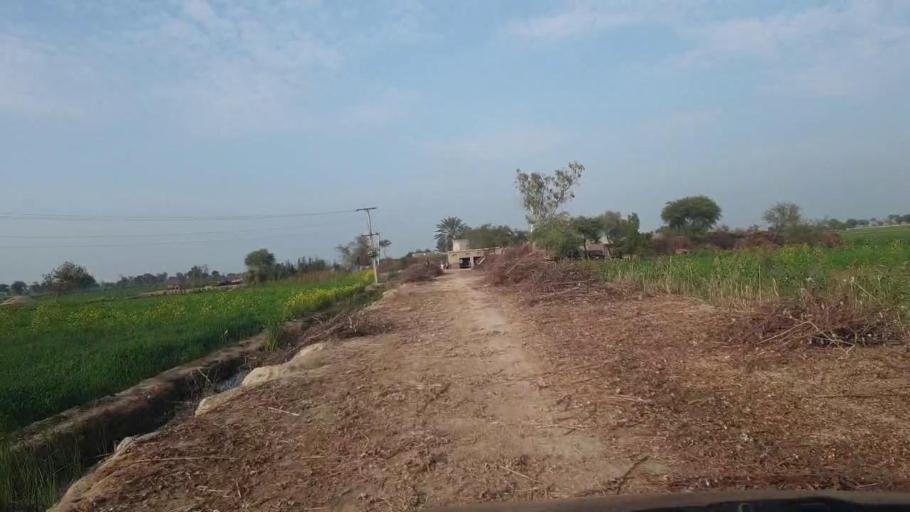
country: PK
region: Sindh
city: Shahdadpur
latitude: 25.8771
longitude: 68.7033
